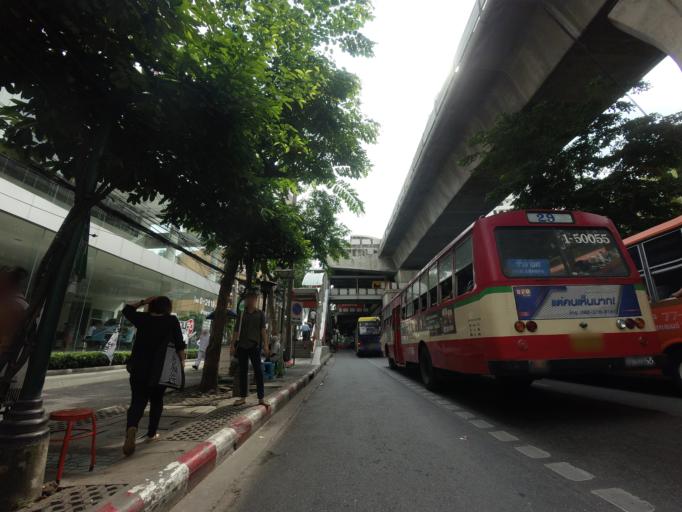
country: TH
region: Bangkok
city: Phaya Thai
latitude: 13.7808
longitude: 100.5452
